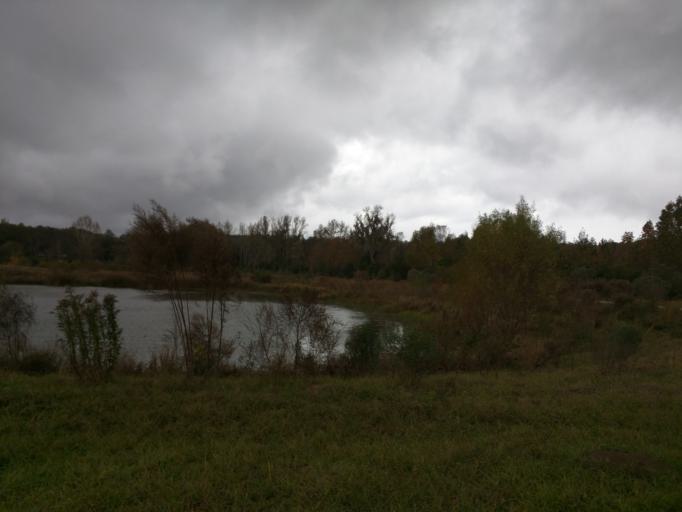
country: US
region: Florida
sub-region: Leon County
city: Tallahassee
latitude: 30.4970
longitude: -84.3093
